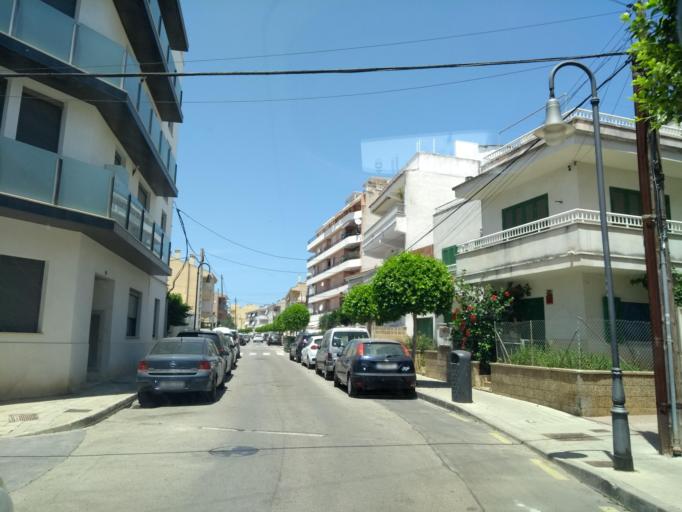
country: ES
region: Balearic Islands
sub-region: Illes Balears
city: Port d'Alcudia
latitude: 39.8394
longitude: 3.1391
